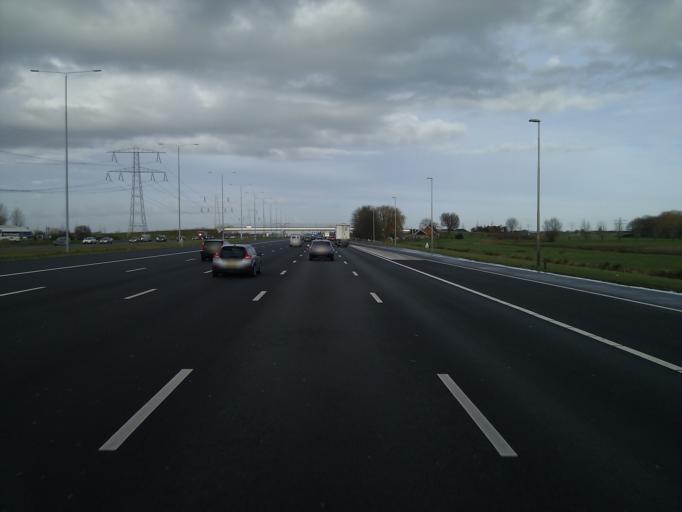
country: NL
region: Utrecht
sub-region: Stichtse Vecht
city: Breukelen
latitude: 52.1860
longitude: 4.9867
